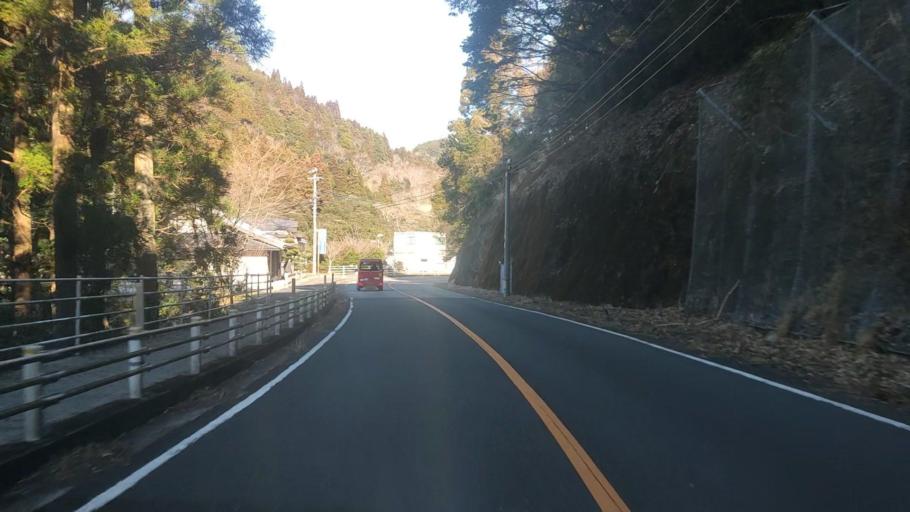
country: JP
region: Oita
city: Saiki
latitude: 32.7681
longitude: 131.8037
